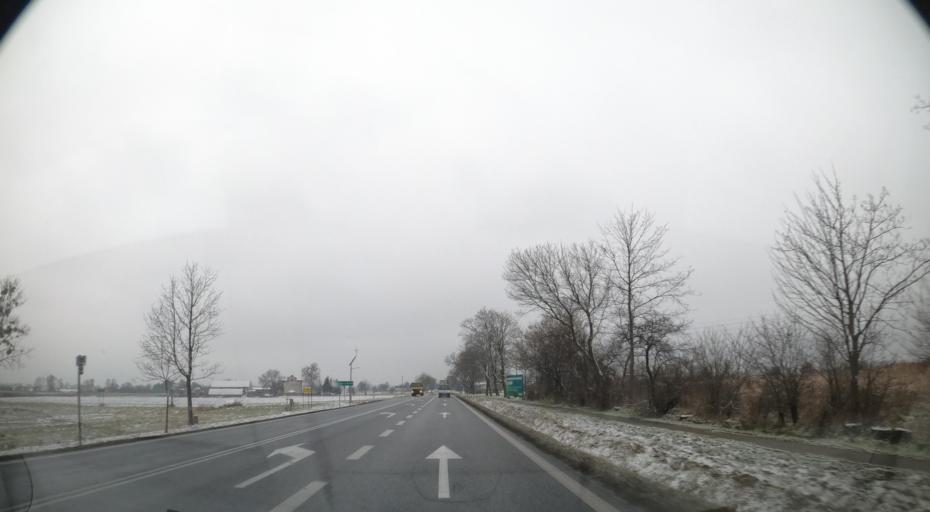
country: PL
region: Masovian Voivodeship
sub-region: Powiat sochaczewski
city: Paprotnia
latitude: 52.2065
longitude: 20.4891
